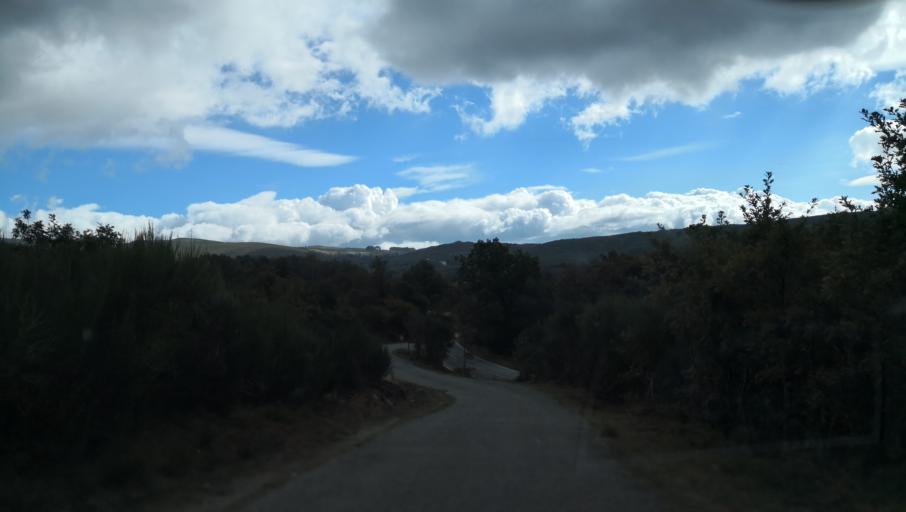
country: PT
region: Vila Real
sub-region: Vila Real
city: Vila Real
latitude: 41.3769
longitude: -7.8084
